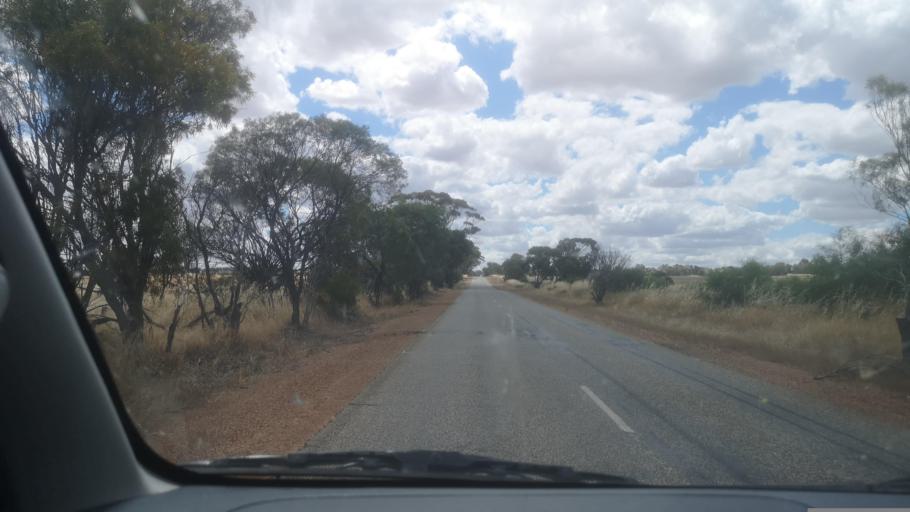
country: AU
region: Western Australia
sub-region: Beverley
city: Beverley
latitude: -31.9777
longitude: 117.0833
